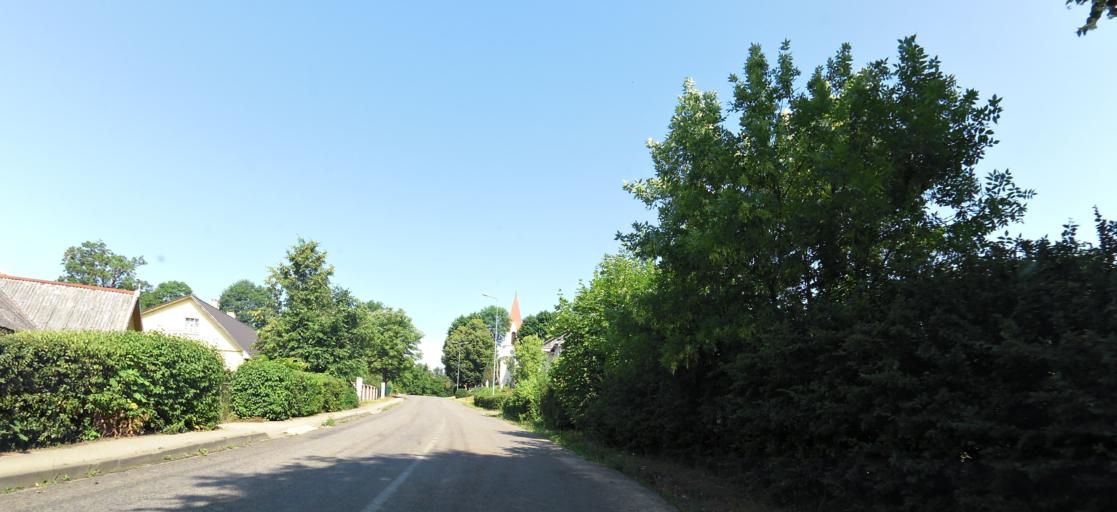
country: LT
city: Grigiskes
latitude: 54.8675
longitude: 25.0668
